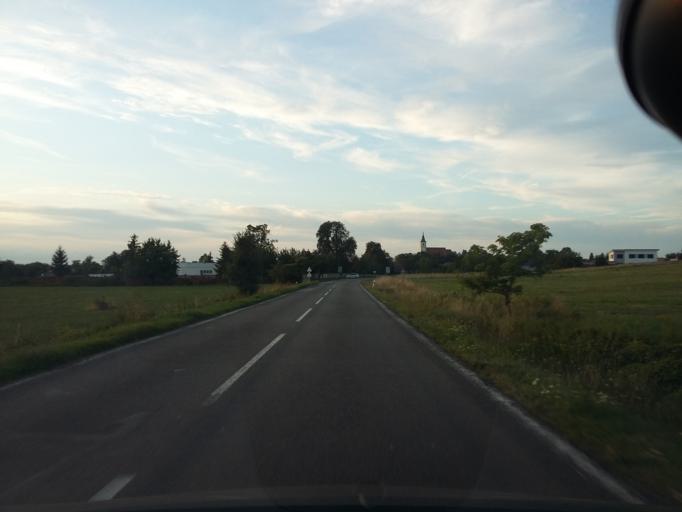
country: SK
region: Bratislavsky
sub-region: Okres Malacky
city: Malacky
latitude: 48.4009
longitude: 17.1551
